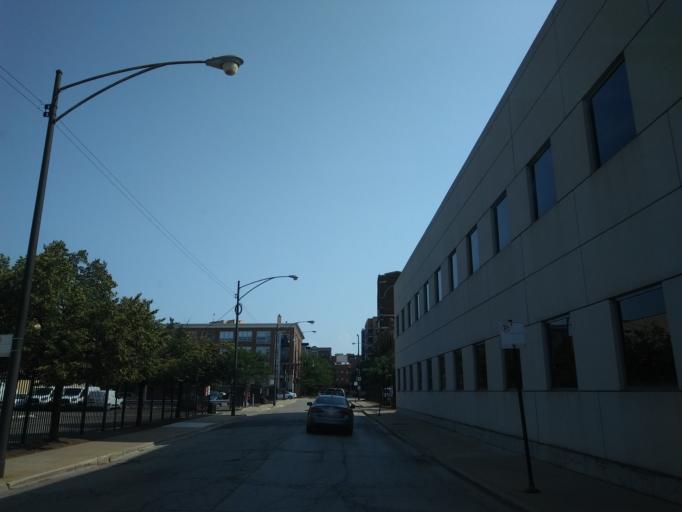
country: US
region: Illinois
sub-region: Cook County
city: Chicago
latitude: 41.8839
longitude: -87.6568
